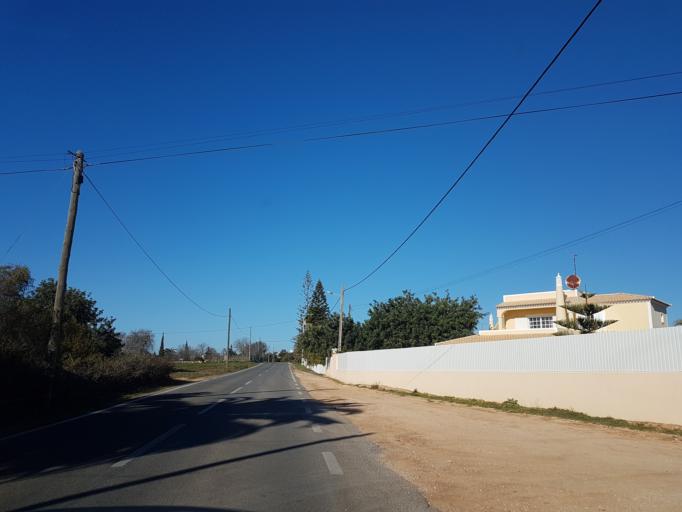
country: PT
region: Faro
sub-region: Lagoa
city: Carvoeiro
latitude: 37.0932
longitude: -8.4316
